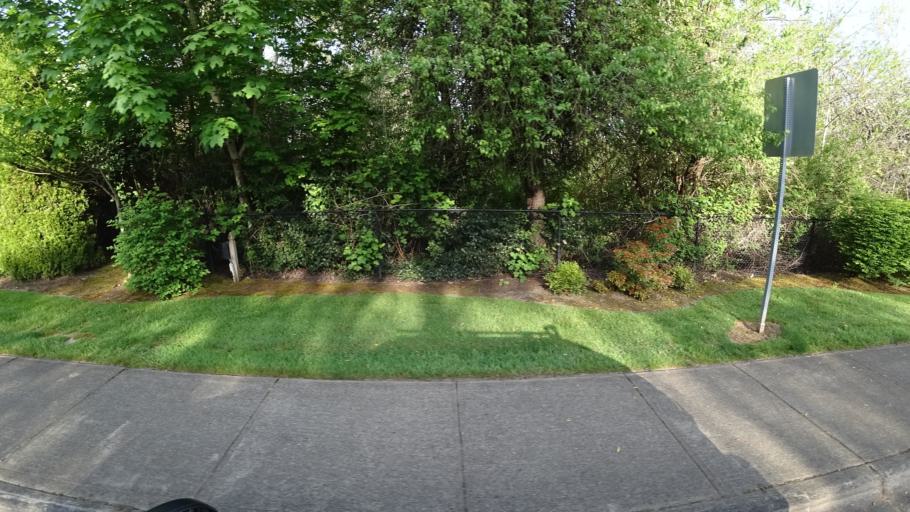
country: US
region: Oregon
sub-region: Washington County
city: King City
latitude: 45.4264
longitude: -122.8387
